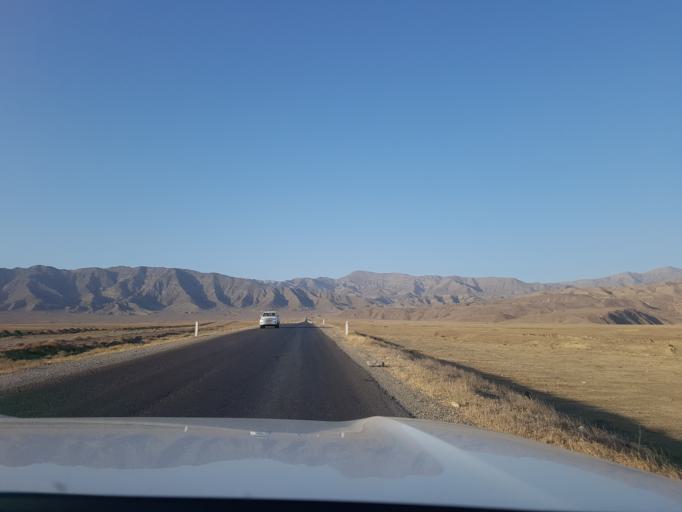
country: TM
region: Ahal
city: Baharly
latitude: 38.5281
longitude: 57.1466
